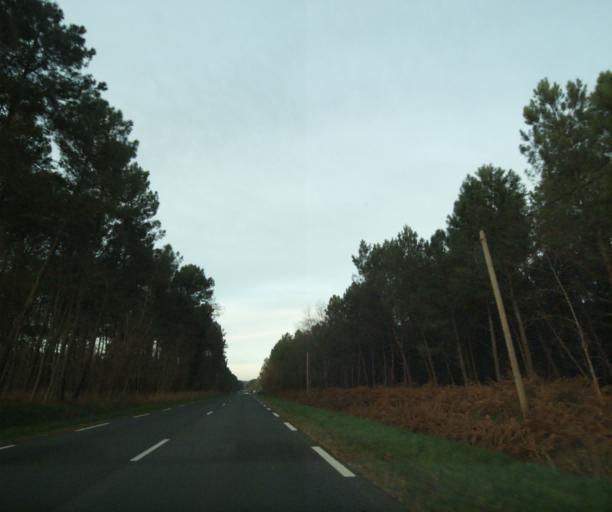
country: FR
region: Aquitaine
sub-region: Departement de la Gironde
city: Bazas
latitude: 44.3421
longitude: -0.2352
